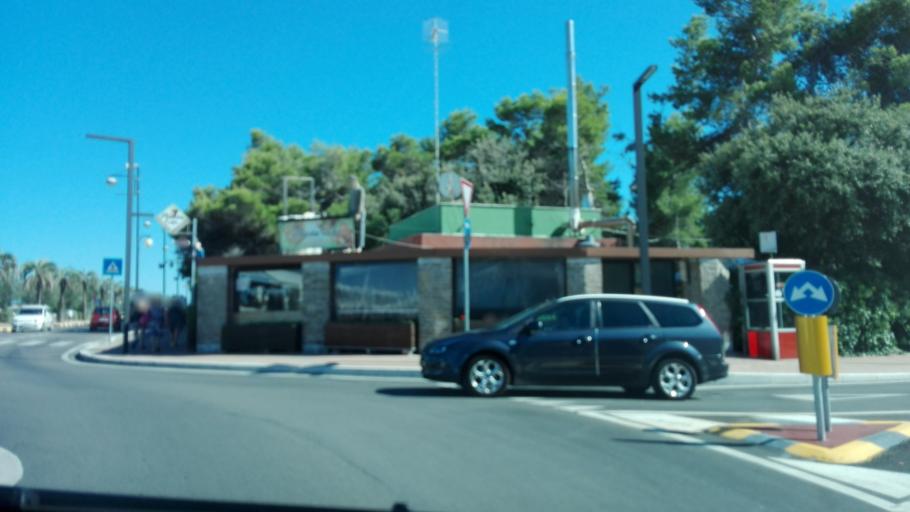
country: IT
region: Abruzzo
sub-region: Provincia di Pescara
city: Montesilvano Marina
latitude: 42.5100
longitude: 14.1689
